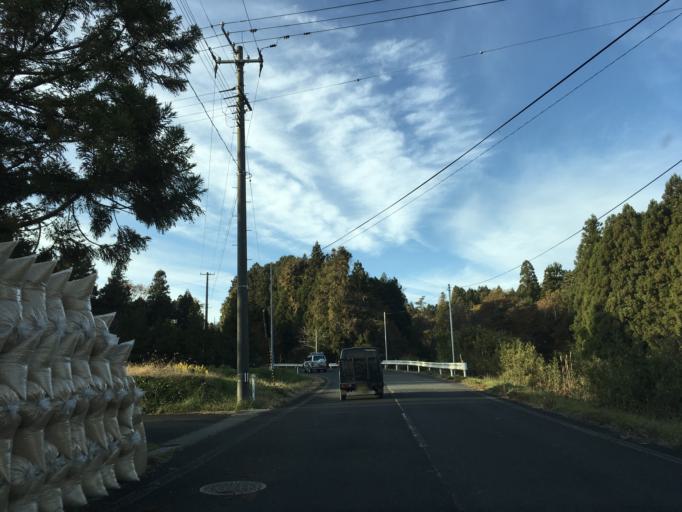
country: JP
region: Iwate
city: Ichinoseki
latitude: 38.8022
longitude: 141.1734
